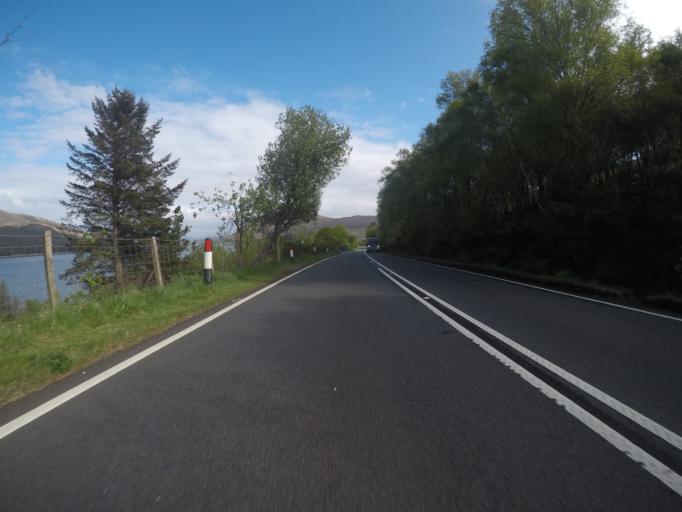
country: GB
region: Scotland
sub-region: Highland
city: Portree
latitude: 57.2761
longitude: -6.0032
